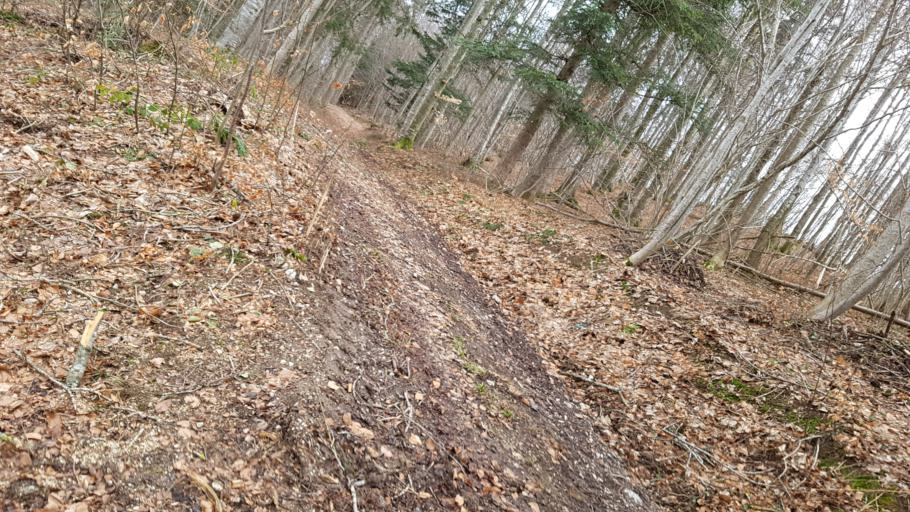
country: AT
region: Salzburg
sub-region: Politischer Bezirk Salzburg-Umgebung
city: Henndorf am Wallersee
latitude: 47.8982
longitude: 13.1677
